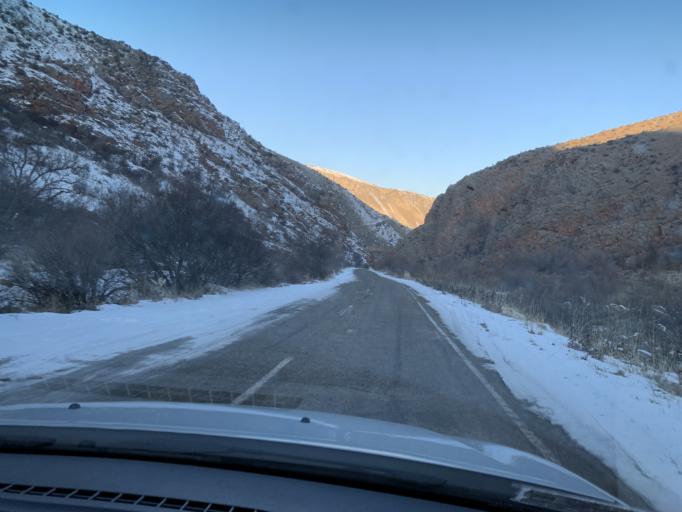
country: AM
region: Vayots' Dzori Marz
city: Areni
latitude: 39.6857
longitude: 45.2264
